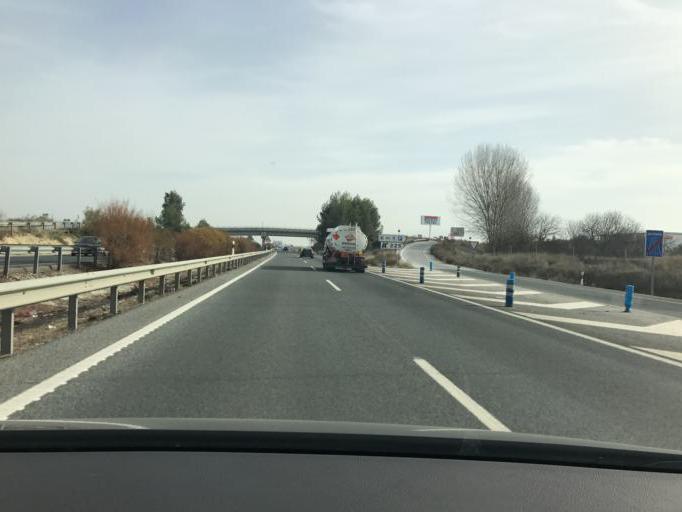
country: ES
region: Andalusia
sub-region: Provincia de Granada
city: Cijuela
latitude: 37.1947
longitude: -3.8057
